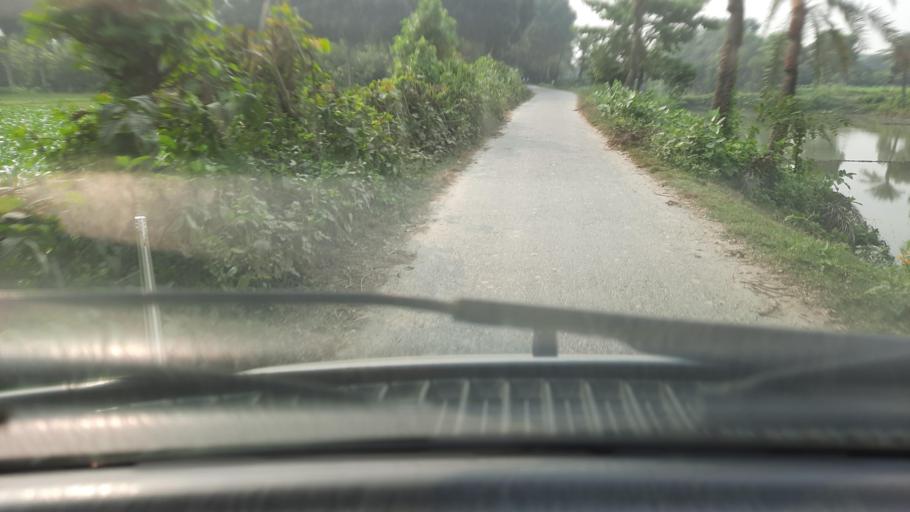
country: BD
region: Khulna
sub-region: Chuadanga
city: Nowlamary
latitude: 23.5998
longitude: 88.8466
